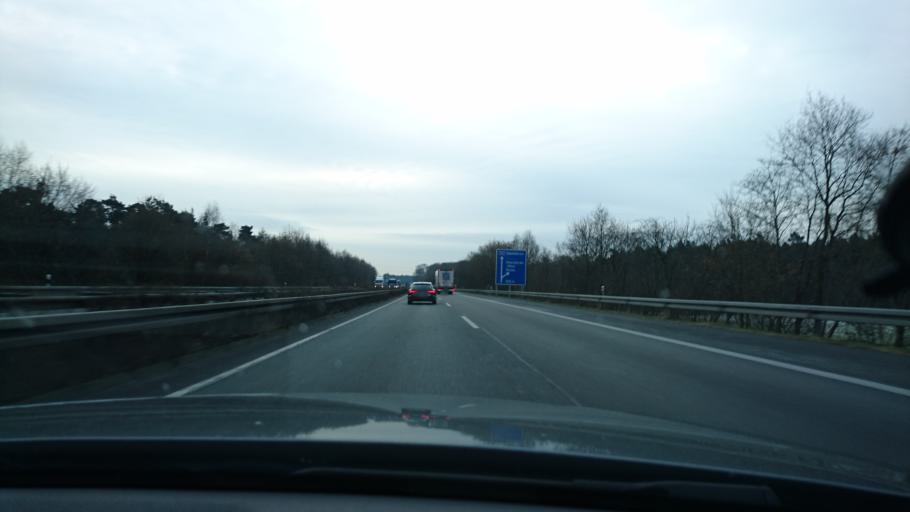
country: DE
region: North Rhine-Westphalia
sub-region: Regierungsbezirk Munster
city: Birgte
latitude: 52.2747
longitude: 7.6486
